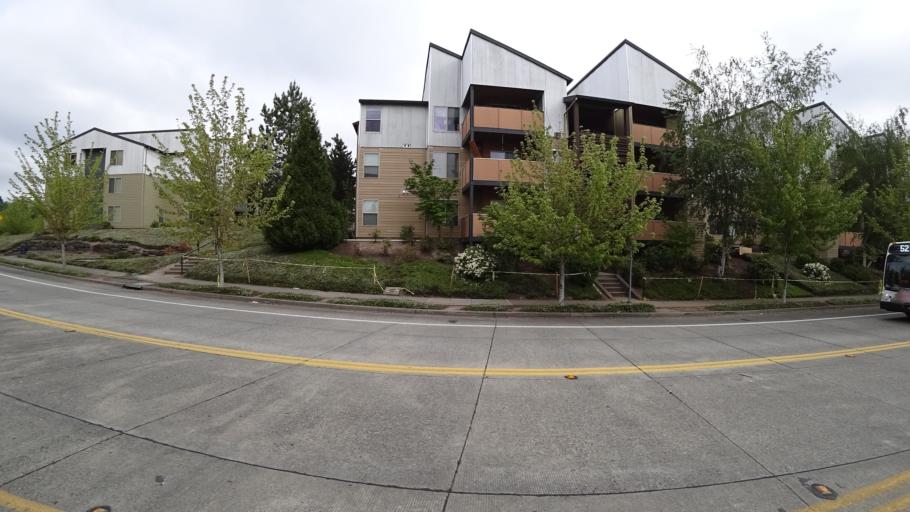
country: US
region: Oregon
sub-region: Washington County
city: Aloha
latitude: 45.5177
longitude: -122.8690
